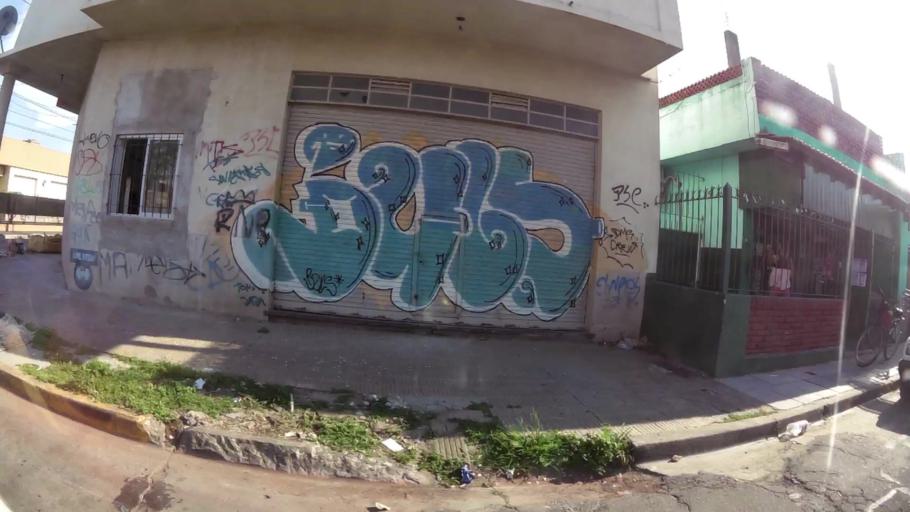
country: AR
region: Buenos Aires
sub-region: Partido de Merlo
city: Merlo
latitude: -34.6590
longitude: -58.7207
